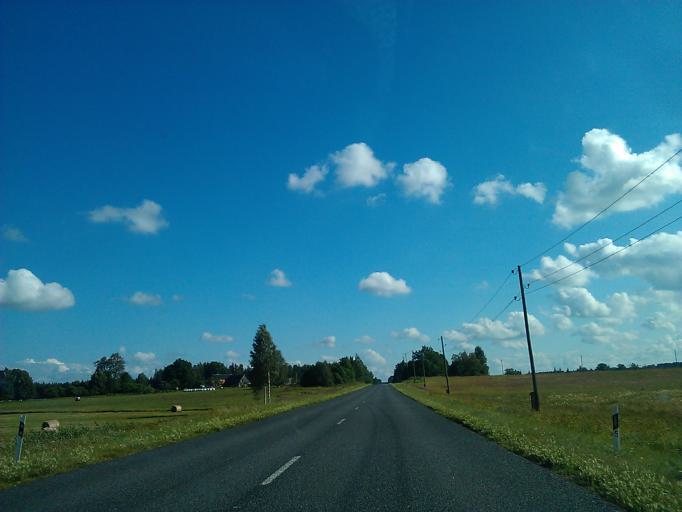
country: LV
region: Naukseni
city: Naukseni
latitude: 57.7664
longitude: 25.4323
